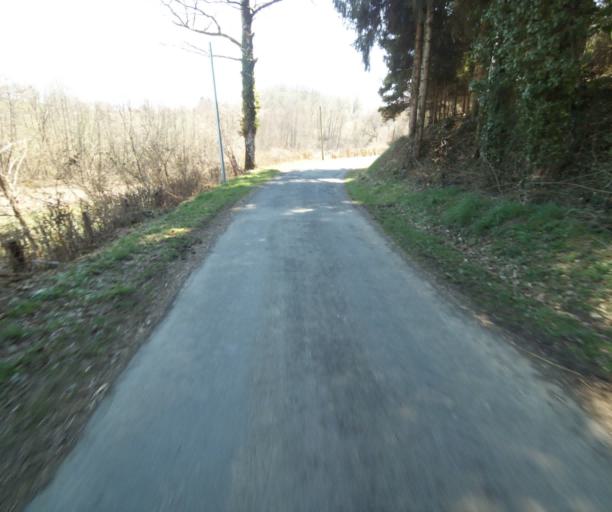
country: FR
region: Limousin
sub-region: Departement de la Correze
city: Saint-Clement
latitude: 45.3240
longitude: 1.7040
